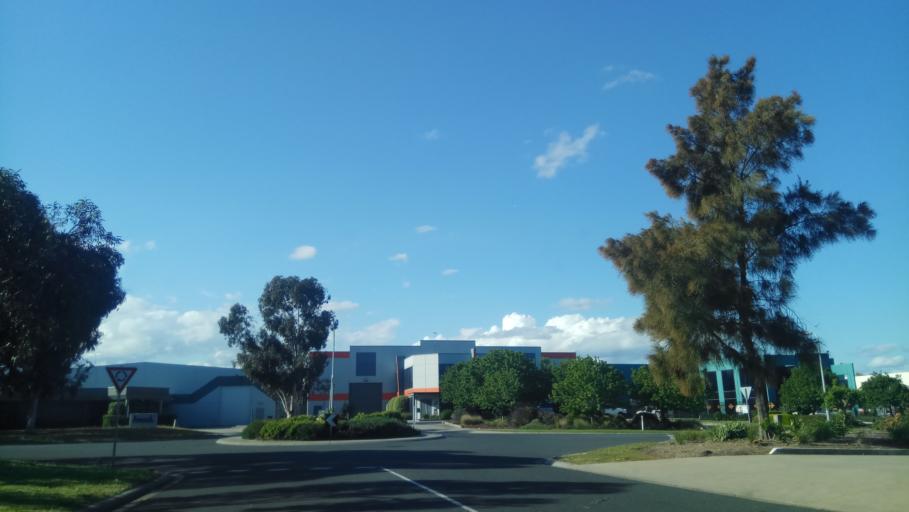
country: AU
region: Victoria
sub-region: Kingston
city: Dingley Village
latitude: -37.9901
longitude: 145.1489
